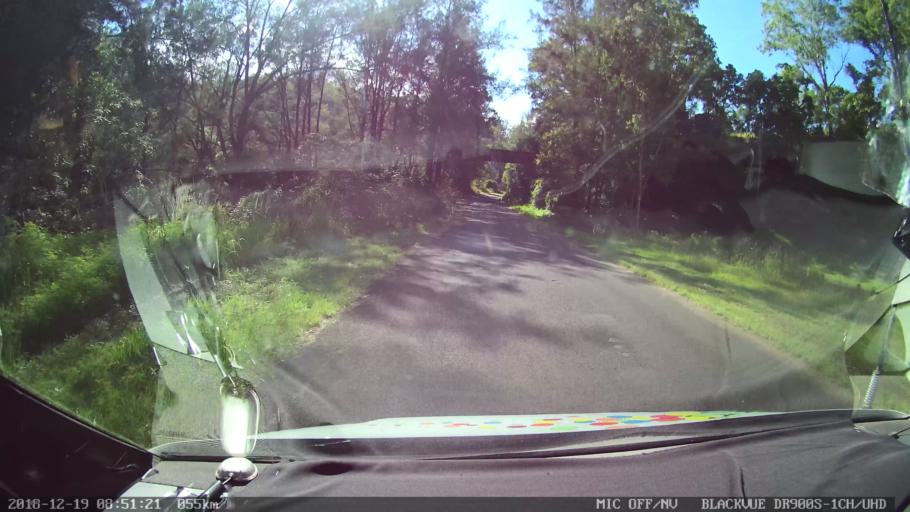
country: AU
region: New South Wales
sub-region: Kyogle
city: Kyogle
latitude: -28.3878
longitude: 152.9780
